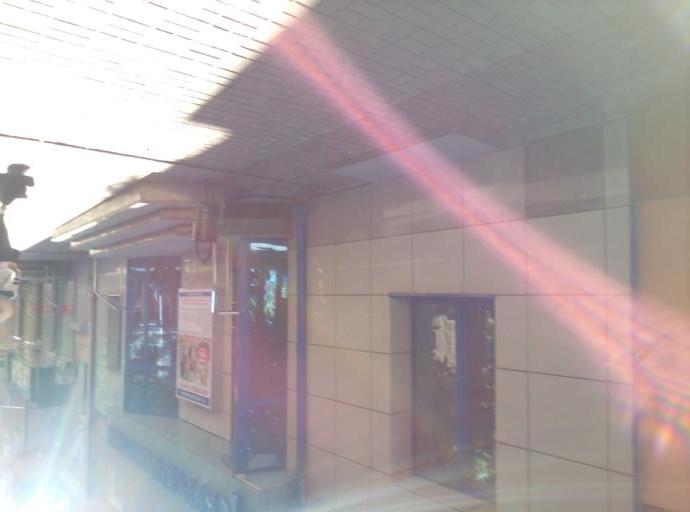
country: RU
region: Kursk
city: Kursk
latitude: 51.7479
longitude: 36.1938
